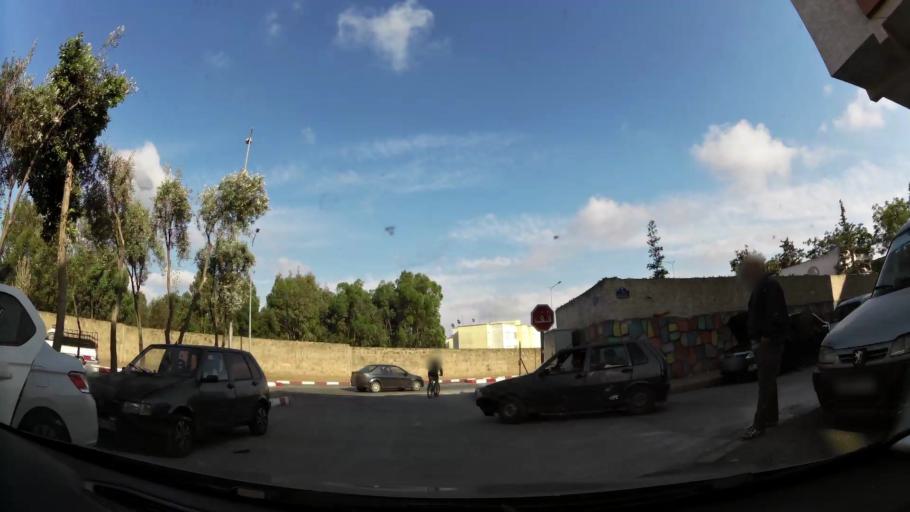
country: MA
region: Rabat-Sale-Zemmour-Zaer
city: Sale
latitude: 34.0510
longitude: -6.7743
